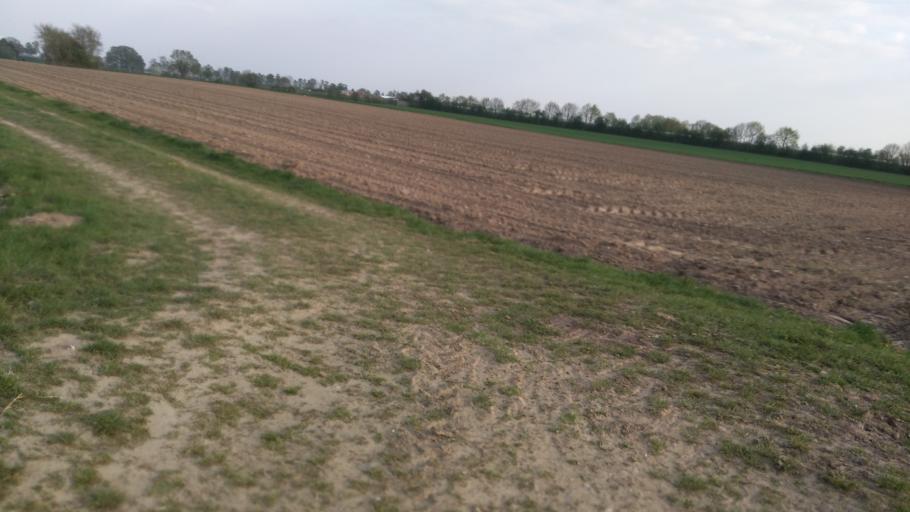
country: DE
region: Lower Saxony
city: Apensen
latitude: 53.4610
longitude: 9.6428
